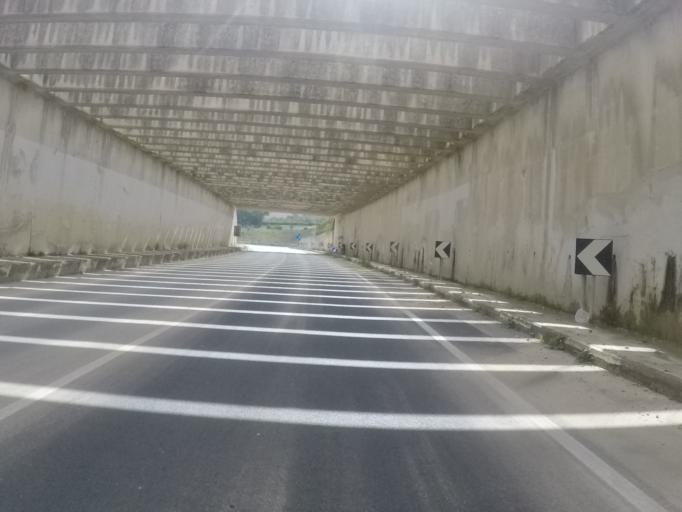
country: IT
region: Sicily
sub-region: Enna
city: Pietraperzia
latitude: 37.4148
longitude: 14.1225
